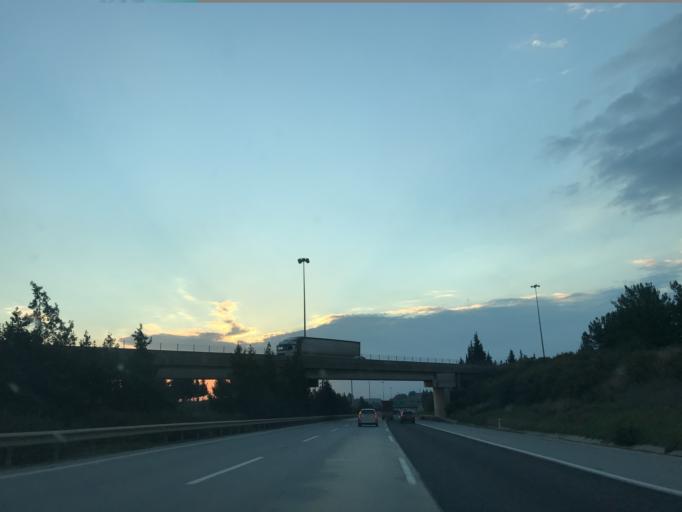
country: TR
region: Mersin
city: Yenice
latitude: 37.0082
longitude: 34.9700
